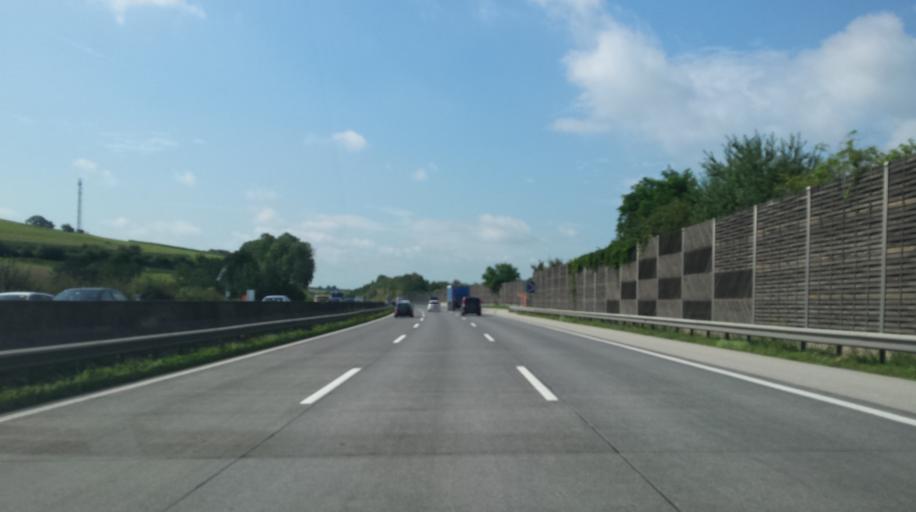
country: AT
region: Lower Austria
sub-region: Politischer Bezirk Melk
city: Erlauf
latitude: 48.1849
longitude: 15.1904
